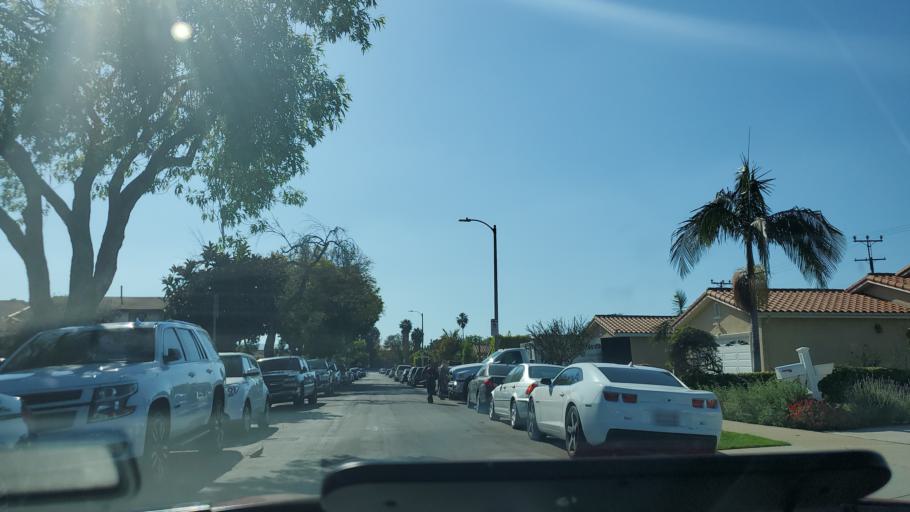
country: US
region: California
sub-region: Los Angeles County
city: West Carson
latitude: 33.7895
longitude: -118.2783
